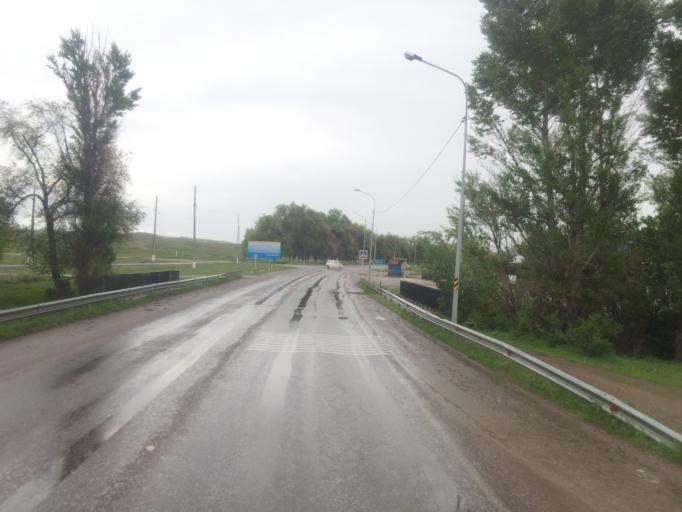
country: KZ
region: Zhambyl
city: Georgiyevka
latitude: 43.2360
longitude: 74.7594
